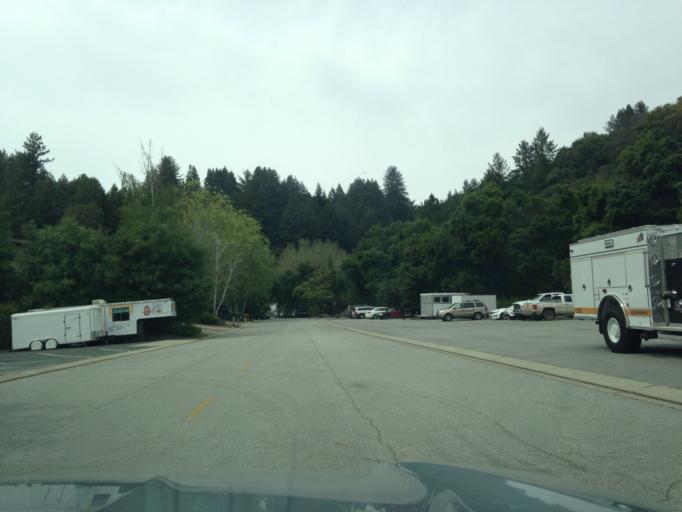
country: US
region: California
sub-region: Santa Cruz County
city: Scotts Valley
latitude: 37.0487
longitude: -122.0195
